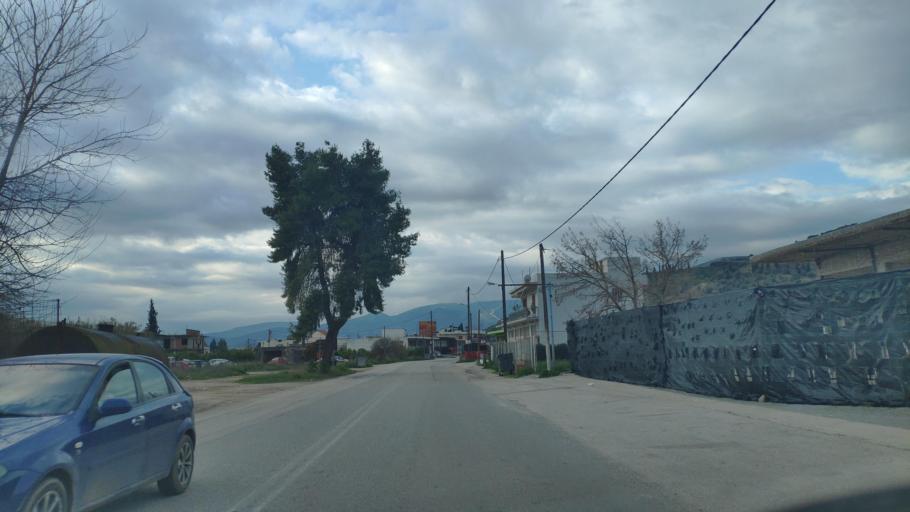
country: GR
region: Peloponnese
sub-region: Nomos Argolidos
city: Argos
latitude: 37.6246
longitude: 22.7167
